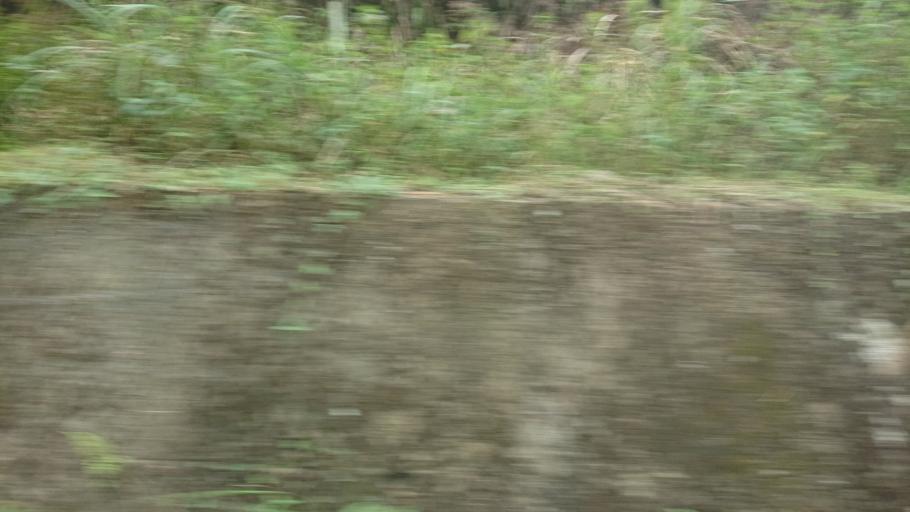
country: TW
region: Taiwan
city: Lugu
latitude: 23.6271
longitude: 120.7092
